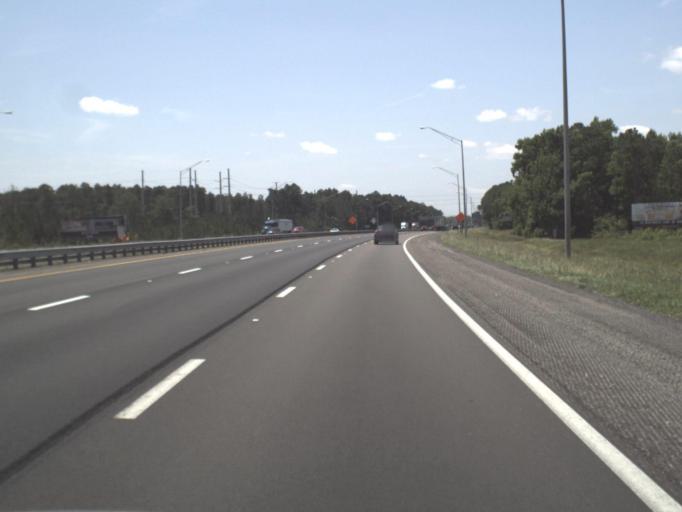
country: US
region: Florida
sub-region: Nassau County
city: Yulee
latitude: 30.5059
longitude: -81.6351
